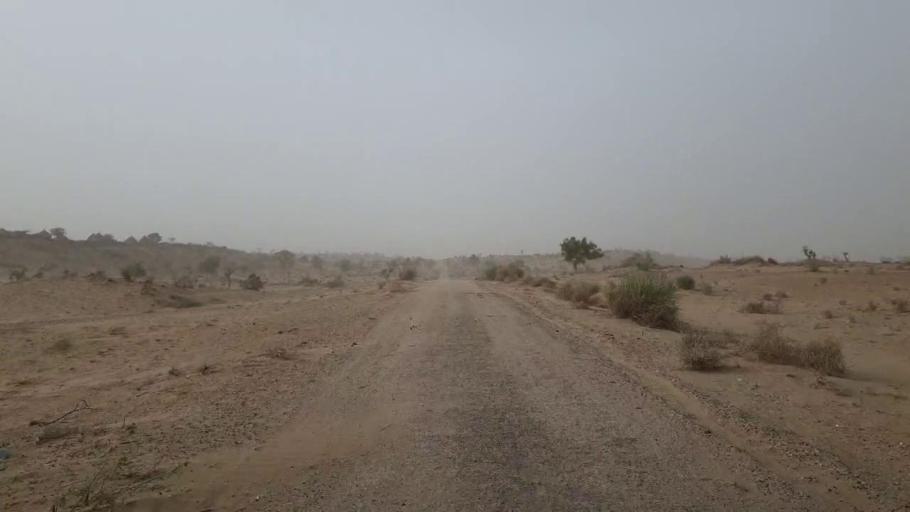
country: PK
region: Sindh
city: Islamkot
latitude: 24.5533
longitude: 70.3607
